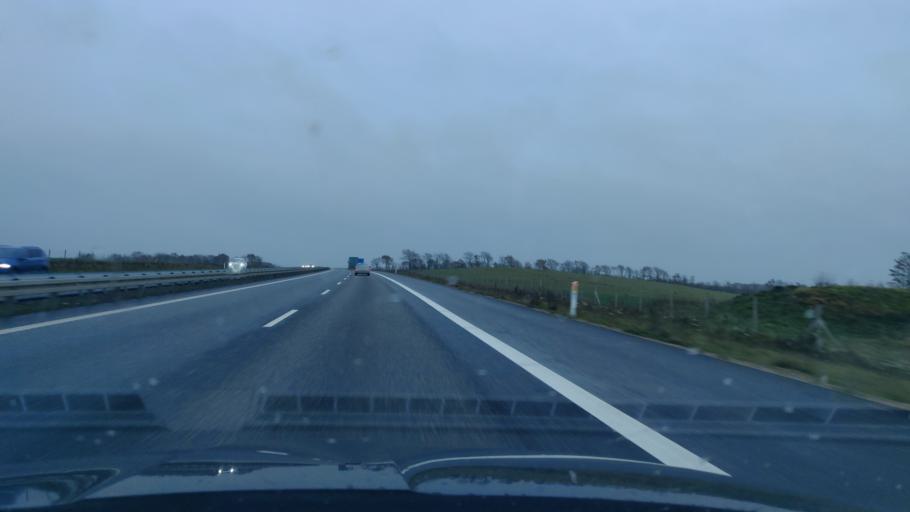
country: DK
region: Central Jutland
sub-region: Herning Kommune
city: Avlum
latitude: 56.2310
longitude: 8.8155
